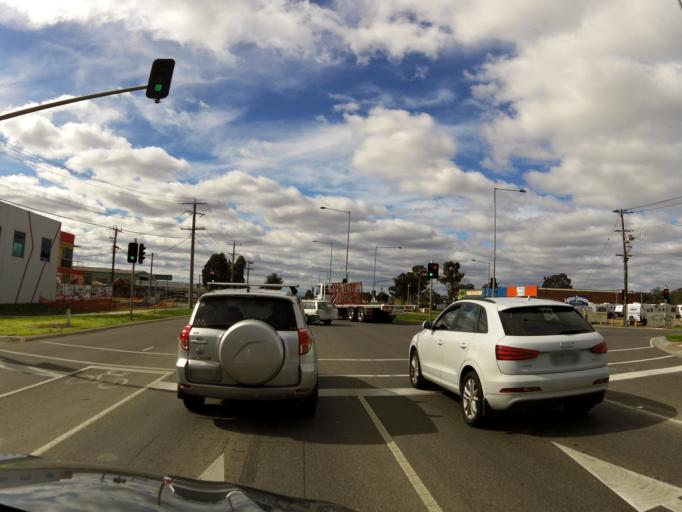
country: AU
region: Victoria
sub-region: Hume
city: Coolaroo
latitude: -37.6451
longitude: 144.9627
